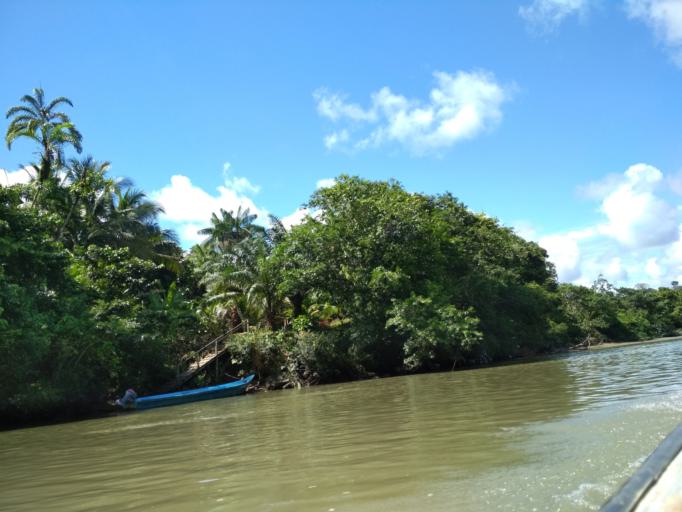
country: CO
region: Cauca
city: Timbiqui
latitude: 2.7577
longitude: -77.6623
